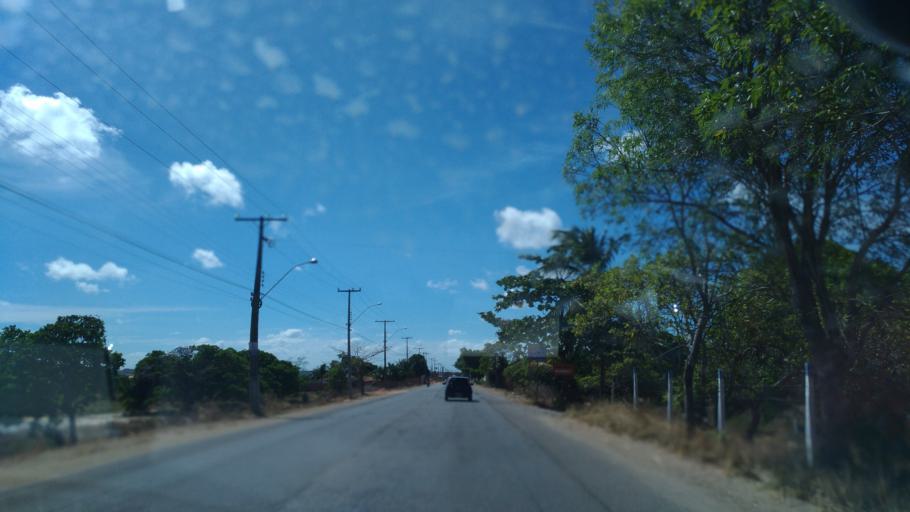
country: BR
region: Alagoas
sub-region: Marechal Deodoro
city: Marechal Deodoro
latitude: -9.7635
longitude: -35.8595
